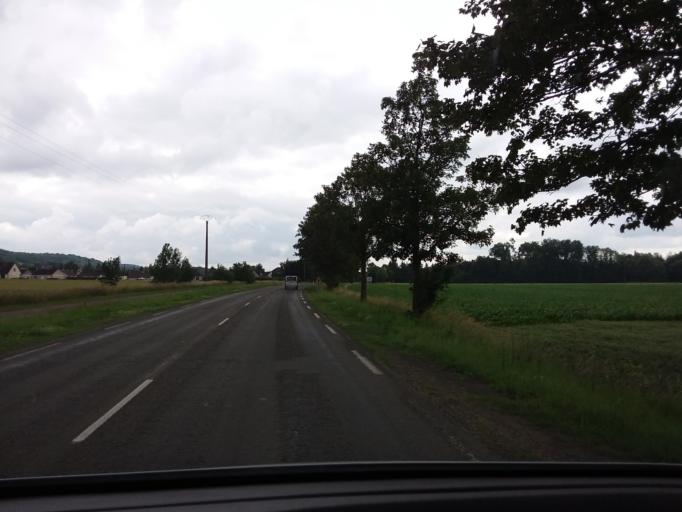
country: FR
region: Picardie
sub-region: Departement de l'Aisne
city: Bucy-le-Long
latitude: 49.3894
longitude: 3.3868
